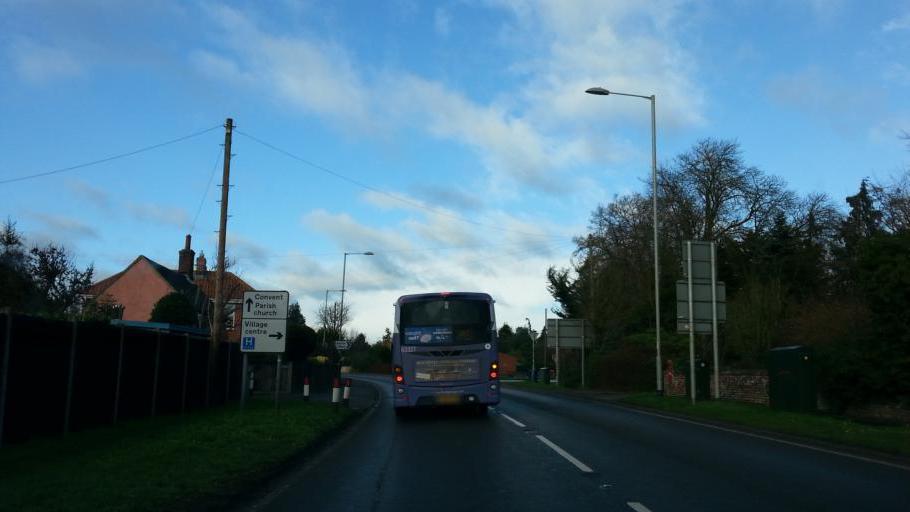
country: GB
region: England
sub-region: Norfolk
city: Ditchingham
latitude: 52.4645
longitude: 1.4417
